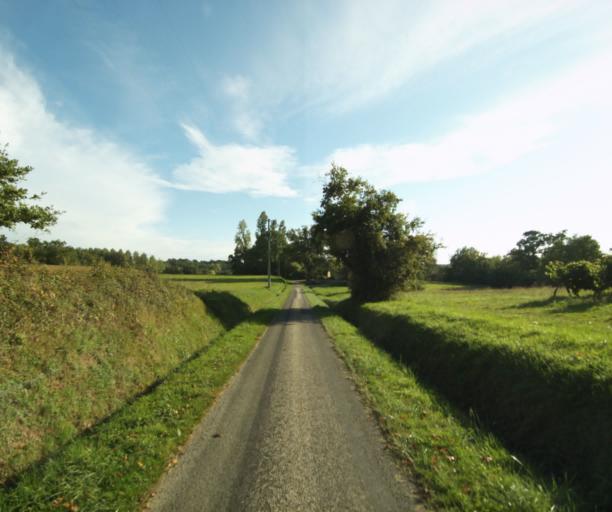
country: FR
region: Midi-Pyrenees
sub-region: Departement du Gers
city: Eauze
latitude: 43.8579
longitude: 0.0314
